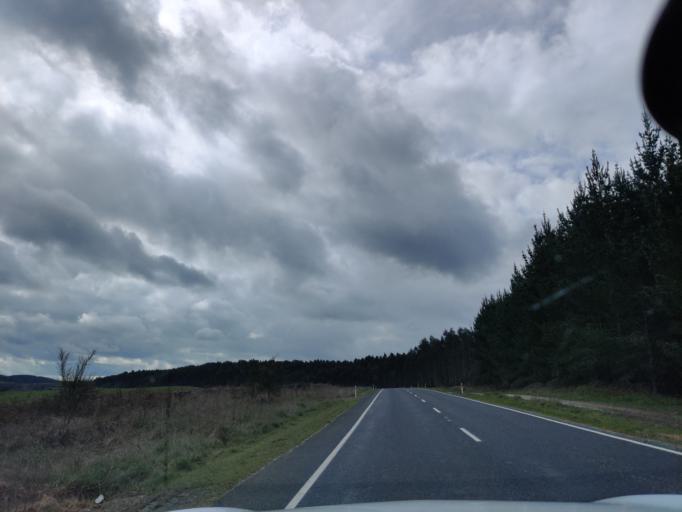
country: NZ
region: Waikato
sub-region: South Waikato District
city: Tokoroa
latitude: -38.3194
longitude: 175.8318
